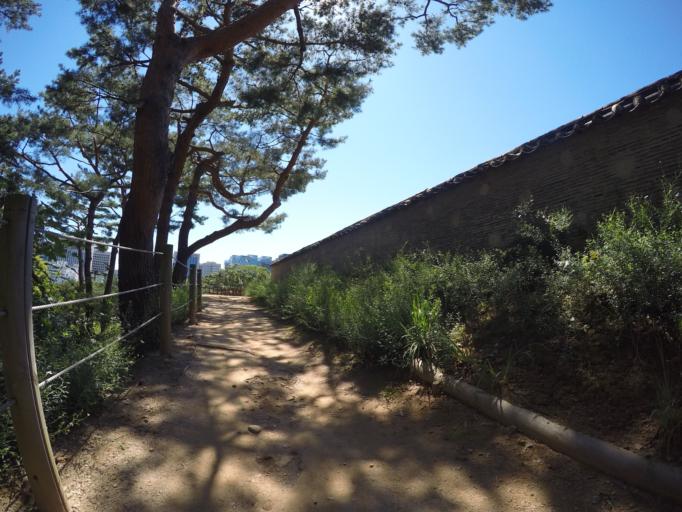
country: KR
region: Seoul
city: Seoul
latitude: 37.5088
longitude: 127.0457
